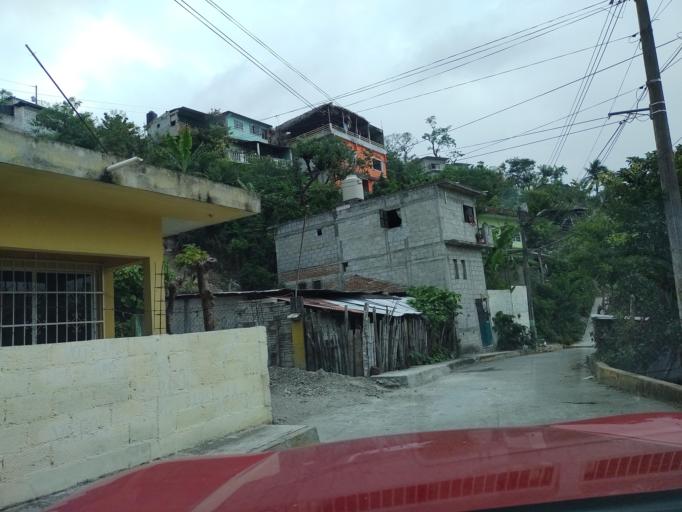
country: MX
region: Veracruz
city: Papantla de Olarte
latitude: 20.4636
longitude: -97.3317
